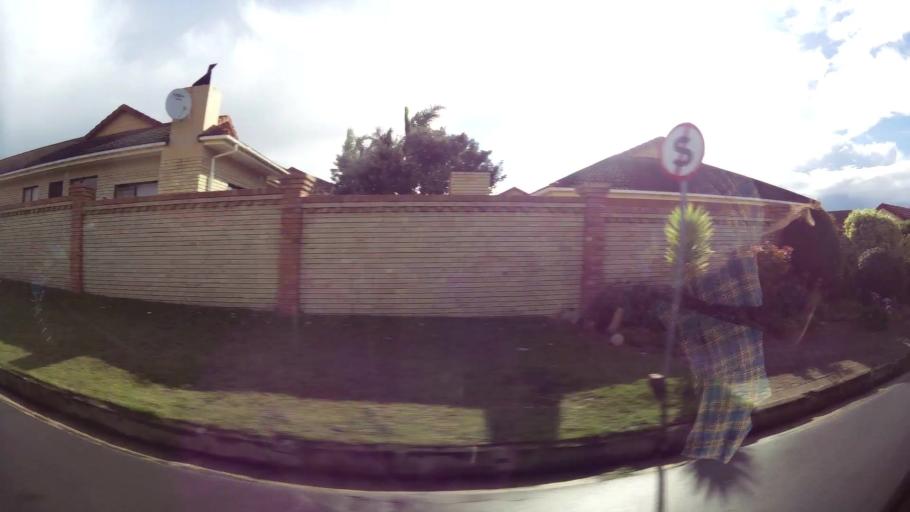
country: ZA
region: Western Cape
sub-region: Eden District Municipality
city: Mossel Bay
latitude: -34.1876
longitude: 22.1320
